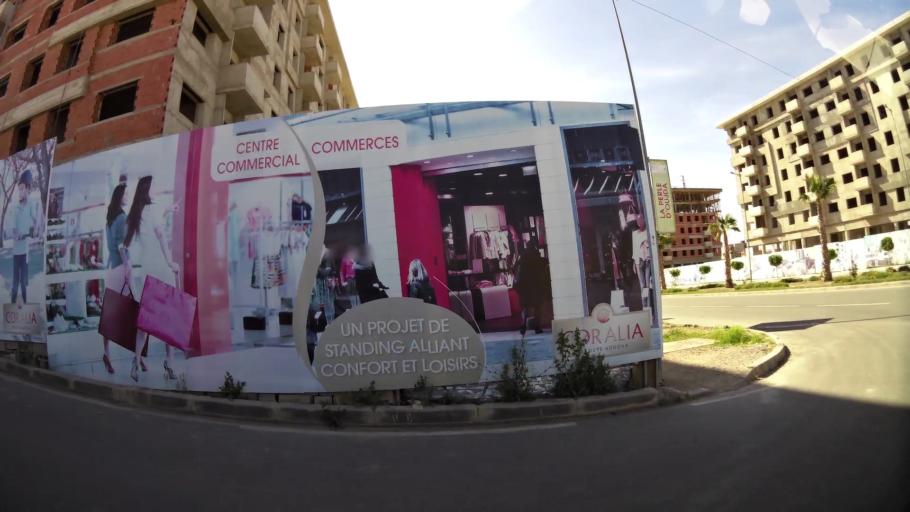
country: MA
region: Oriental
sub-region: Oujda-Angad
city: Oujda
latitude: 34.6637
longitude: -1.9132
